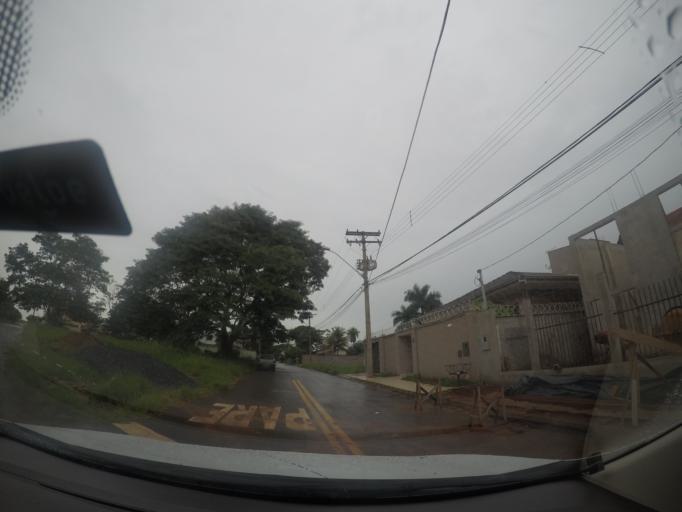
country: BR
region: Goias
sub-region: Goiania
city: Goiania
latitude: -16.6444
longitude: -49.2306
